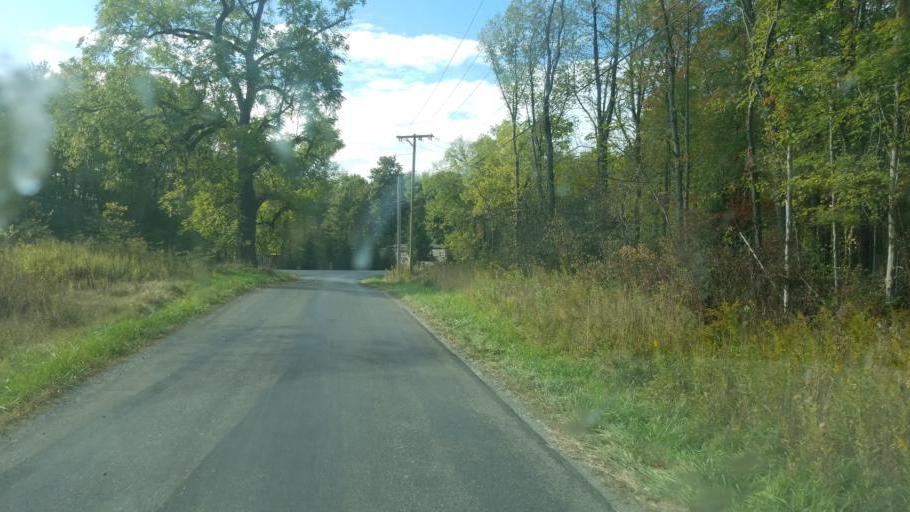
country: US
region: Pennsylvania
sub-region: Mercer County
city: Mercer
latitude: 41.3296
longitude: -80.2453
